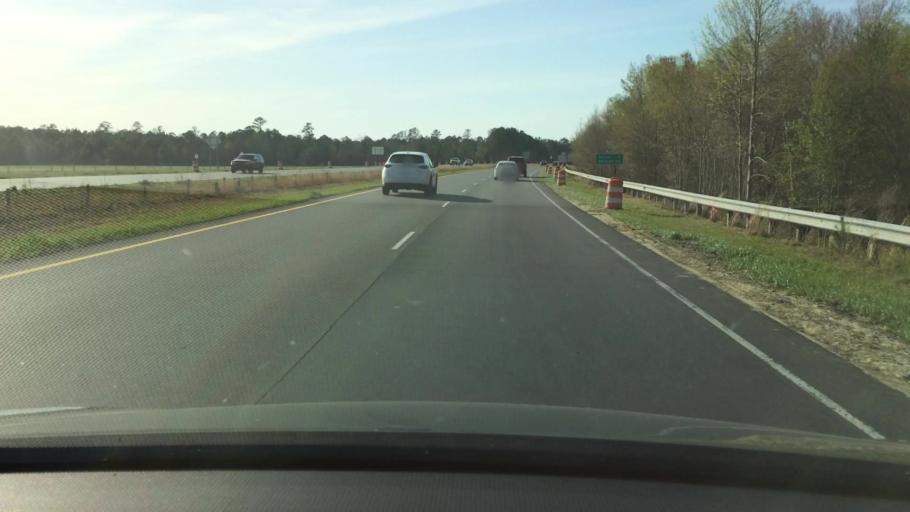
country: US
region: North Carolina
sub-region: Johnston County
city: Pine Level
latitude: 35.4924
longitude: -78.2719
